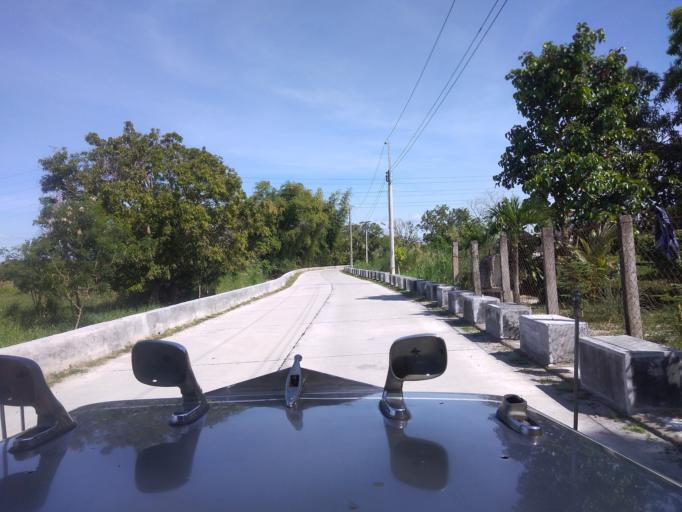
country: PH
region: Central Luzon
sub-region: Province of Pampanga
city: Magliman
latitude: 15.0260
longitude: 120.6656
